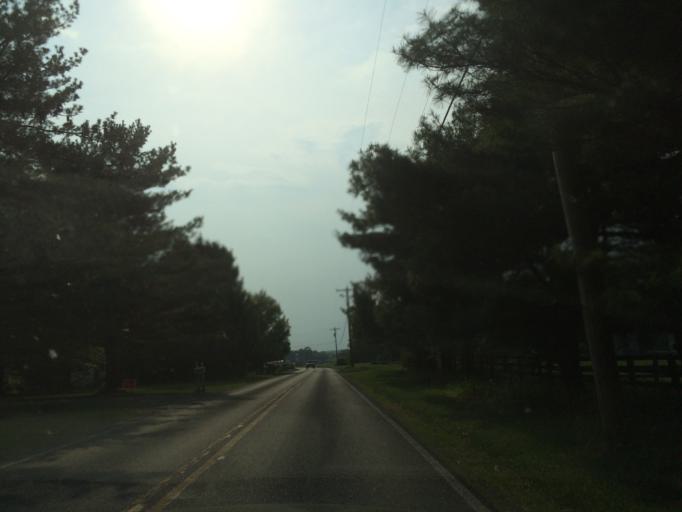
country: US
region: Maryland
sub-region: Carroll County
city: Mount Airy
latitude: 39.3523
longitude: -77.0852
